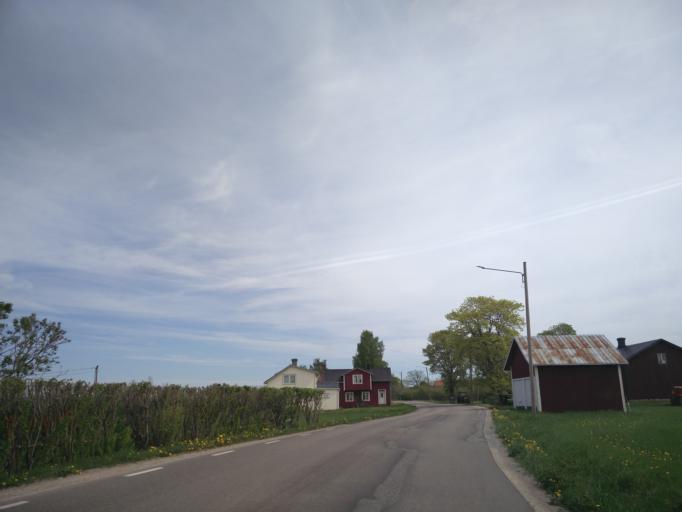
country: SE
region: Gaevleborg
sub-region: Hudiksvalls Kommun
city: Sorforsa
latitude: 61.7674
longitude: 17.0012
